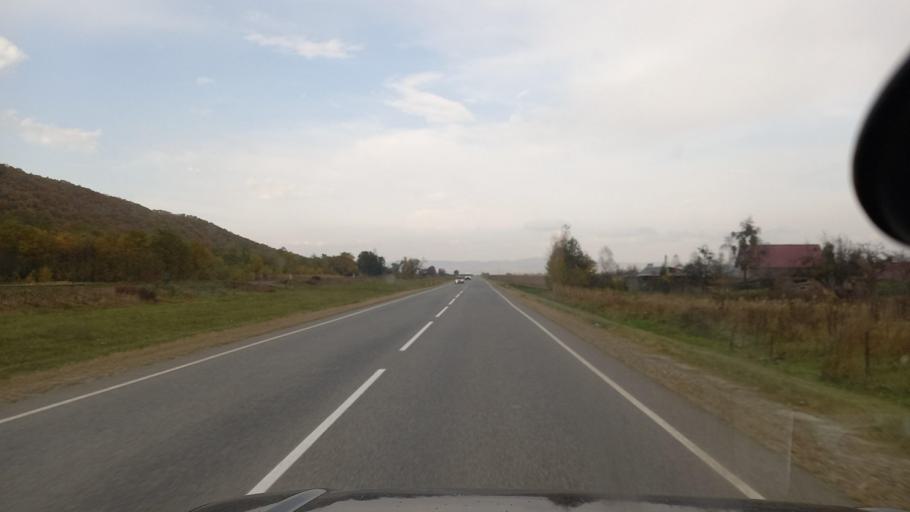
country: RU
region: Krasnodarskiy
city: Shedok
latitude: 44.2399
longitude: 40.8600
